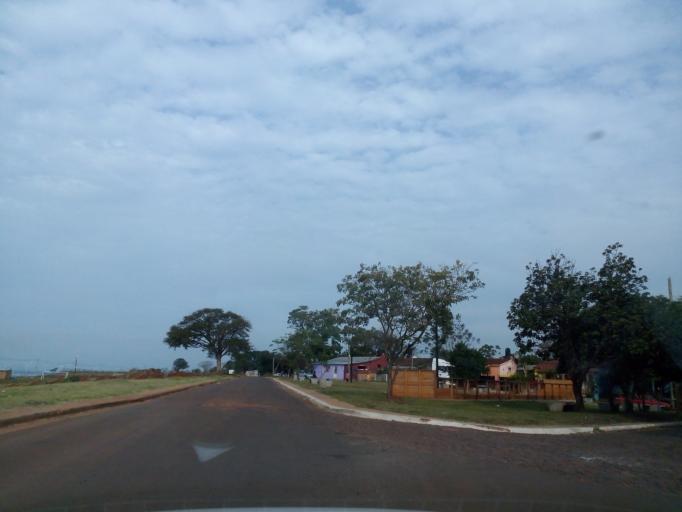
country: AR
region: Misiones
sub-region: Departamento de Capital
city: Posadas
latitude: -27.4194
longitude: -55.8825
